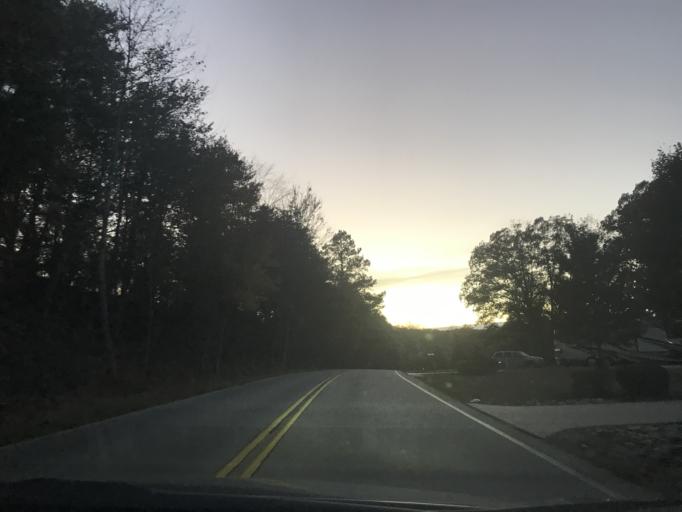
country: US
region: South Carolina
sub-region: Spartanburg County
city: Mayo
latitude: 35.0881
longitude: -81.8902
